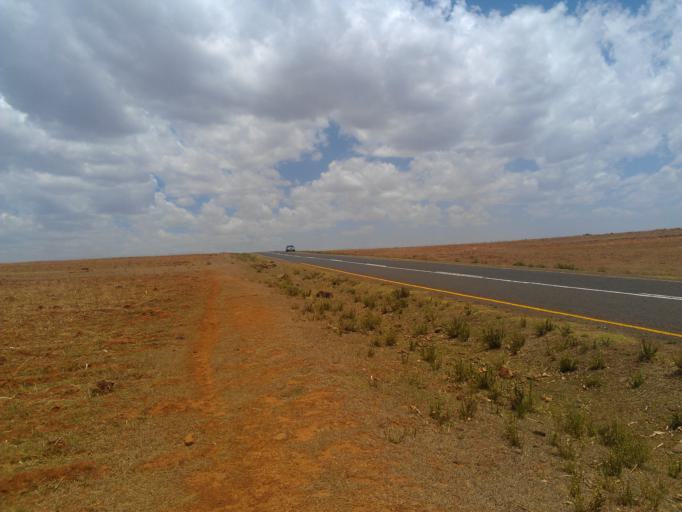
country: LS
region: Berea
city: Teyateyaneng
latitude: -29.2705
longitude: 27.6831
